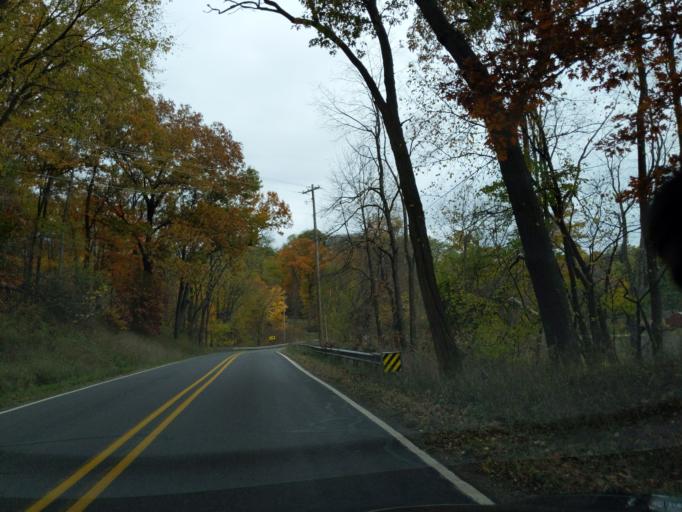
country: US
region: Michigan
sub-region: Jackson County
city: Spring Arbor
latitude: 42.3320
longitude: -84.6001
